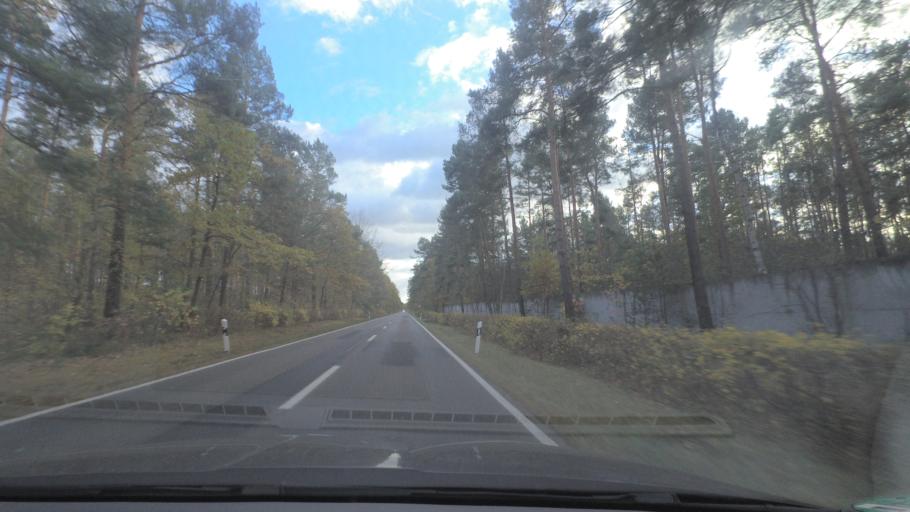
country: DE
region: Brandenburg
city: Sperenberg
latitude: 52.1075
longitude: 13.3722
